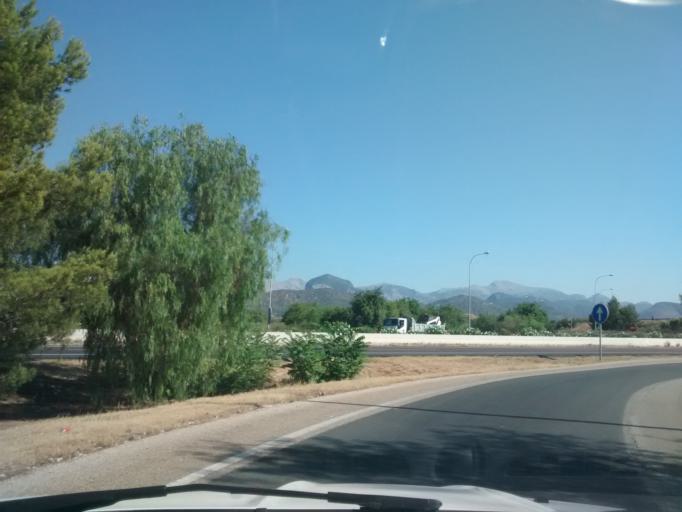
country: ES
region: Balearic Islands
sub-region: Illes Balears
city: Consell
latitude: 39.6685
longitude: 2.8241
